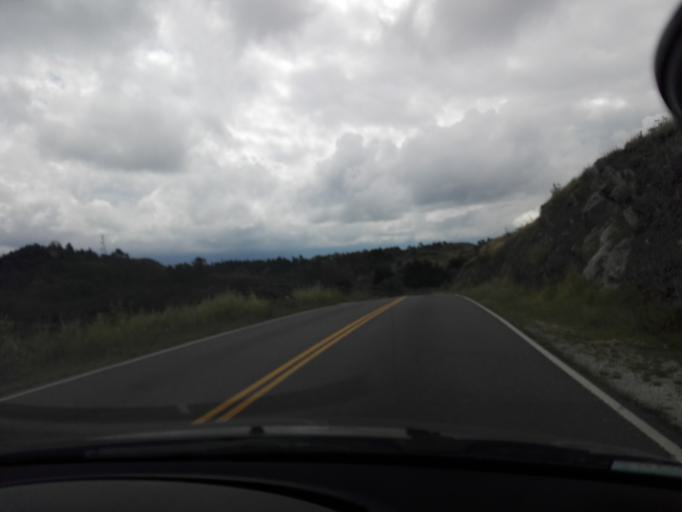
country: AR
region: Cordoba
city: Cuesta Blanca
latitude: -31.5969
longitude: -64.5410
